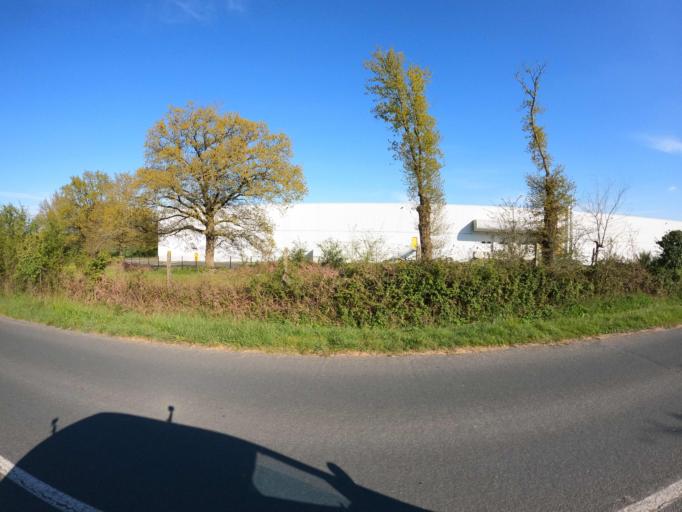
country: FR
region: Pays de la Loire
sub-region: Departement de la Vendee
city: Mortagne-sur-Sevre
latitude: 46.9793
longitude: -0.9648
